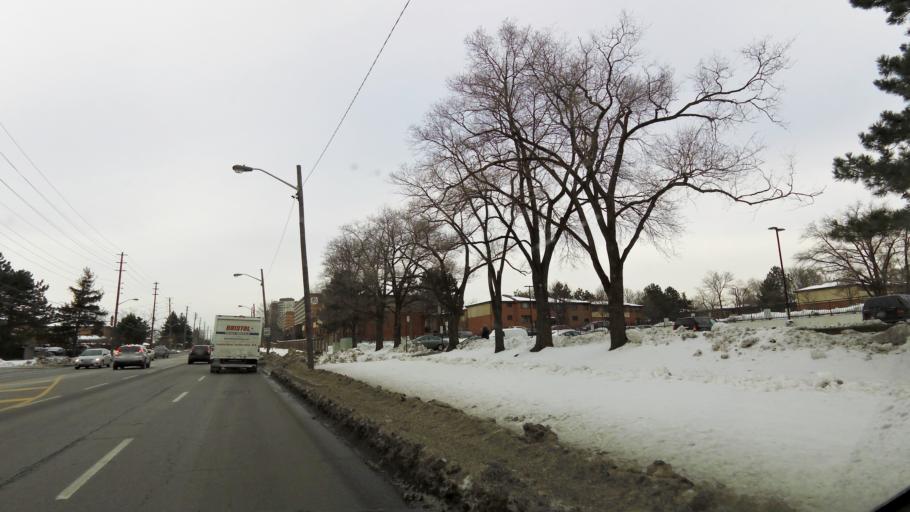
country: CA
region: Ontario
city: Etobicoke
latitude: 43.6983
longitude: -79.5472
